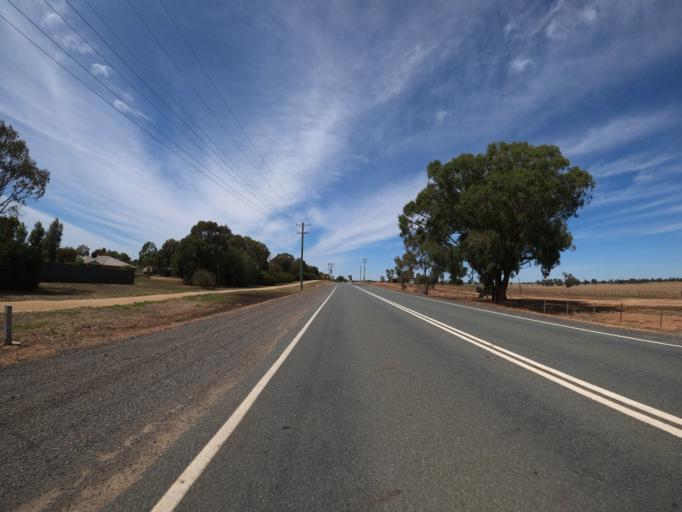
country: AU
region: Victoria
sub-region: Moira
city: Yarrawonga
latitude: -36.0460
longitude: 145.9955
